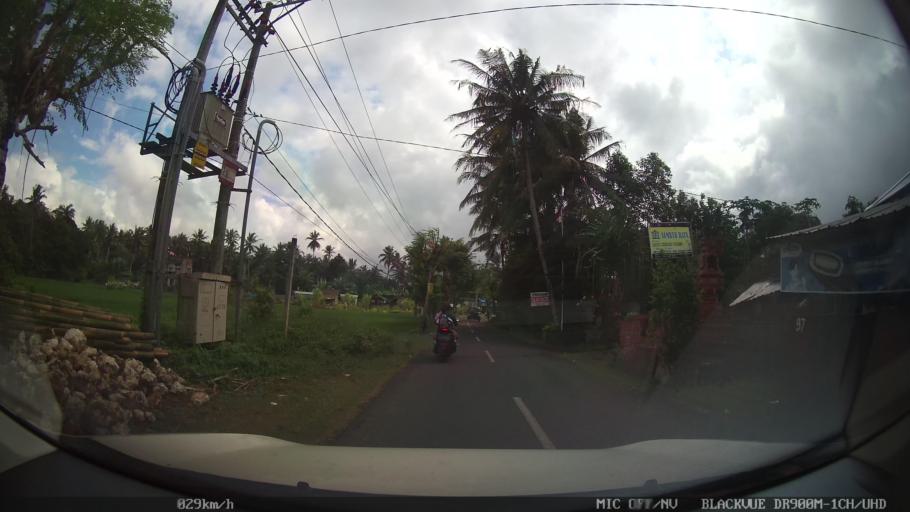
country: ID
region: Bali
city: Banjar Bucu
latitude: -8.5748
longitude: 115.2033
